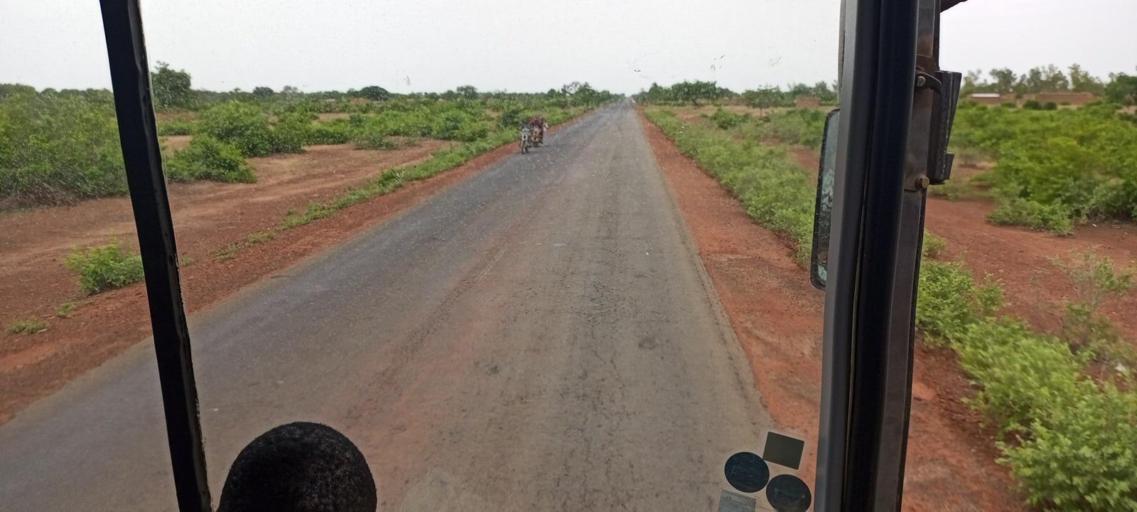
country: ML
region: Sikasso
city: Koutiala
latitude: 12.5485
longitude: -5.5825
